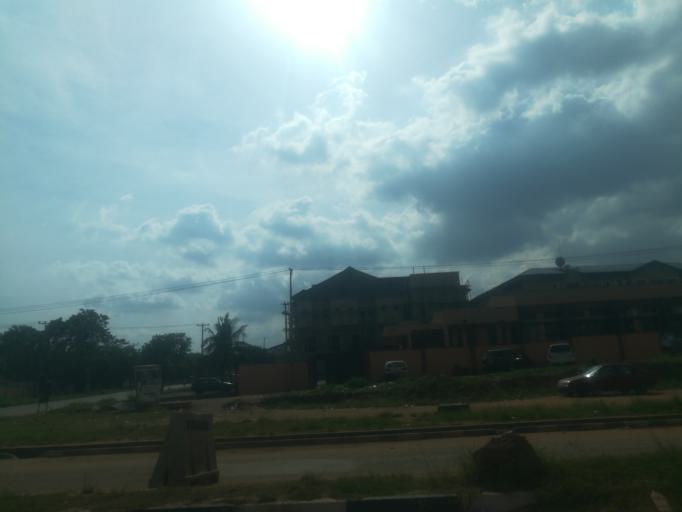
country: NG
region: Ogun
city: Abeokuta
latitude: 7.1320
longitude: 3.3536
